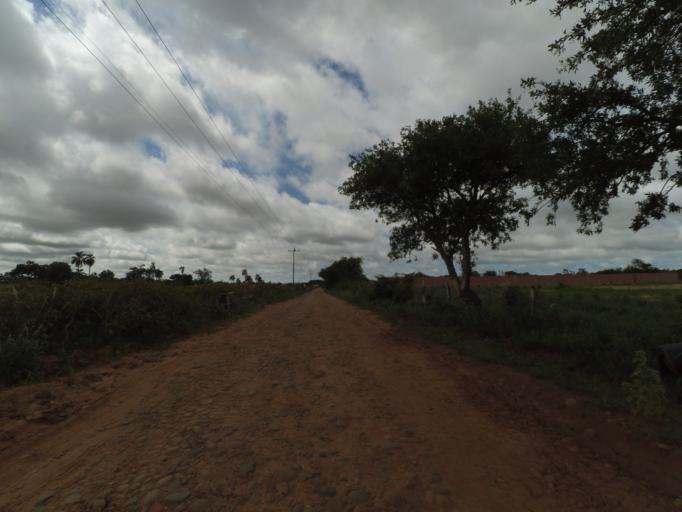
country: BO
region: Santa Cruz
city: Santa Rita
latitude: -17.9018
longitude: -63.2425
